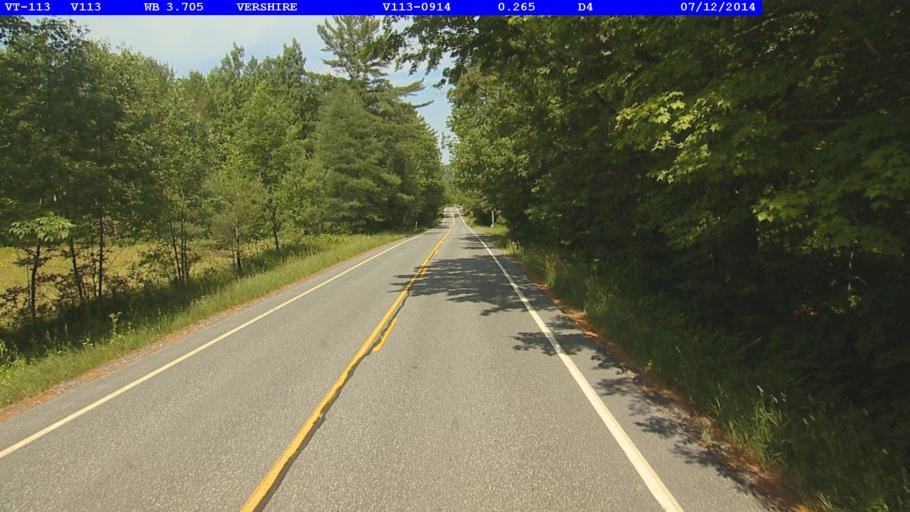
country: US
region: Vermont
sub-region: Orange County
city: Chelsea
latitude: 43.9909
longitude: -72.3793
